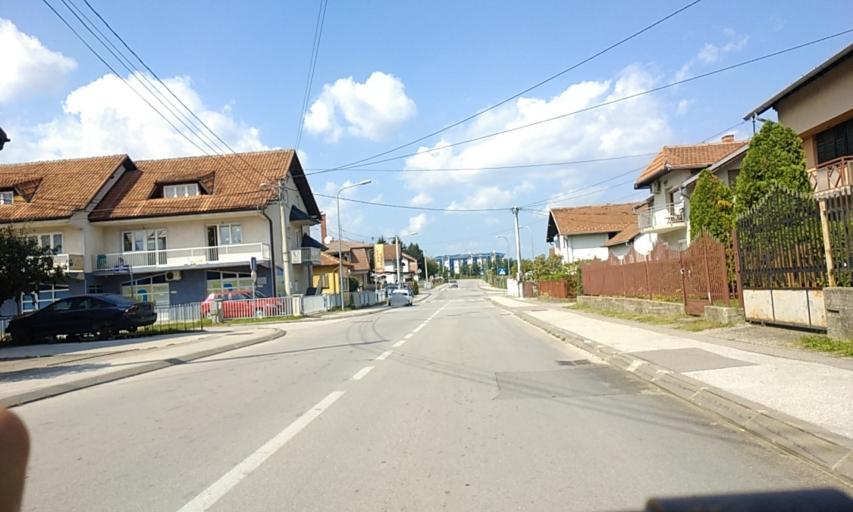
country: BA
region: Republika Srpska
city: Banja Luka
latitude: 44.7900
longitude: 17.1940
